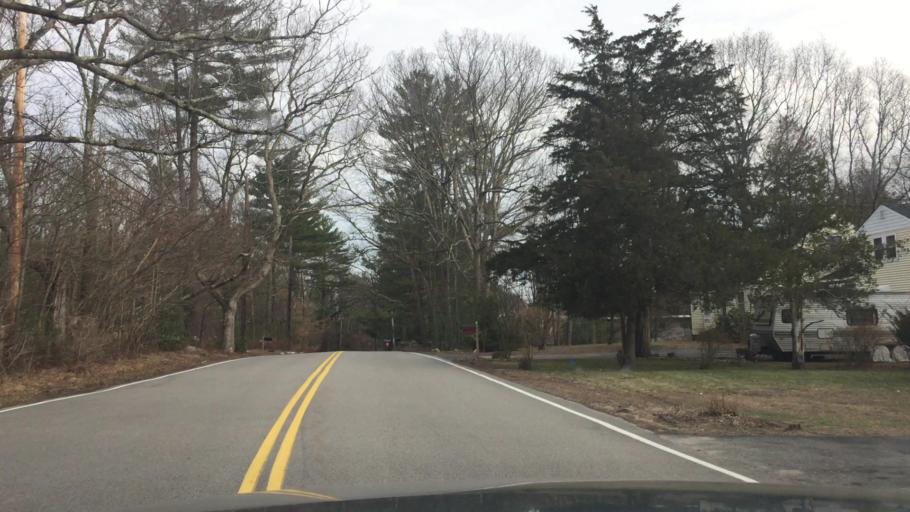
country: US
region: Massachusetts
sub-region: Norfolk County
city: Medway
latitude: 42.1417
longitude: -71.4539
